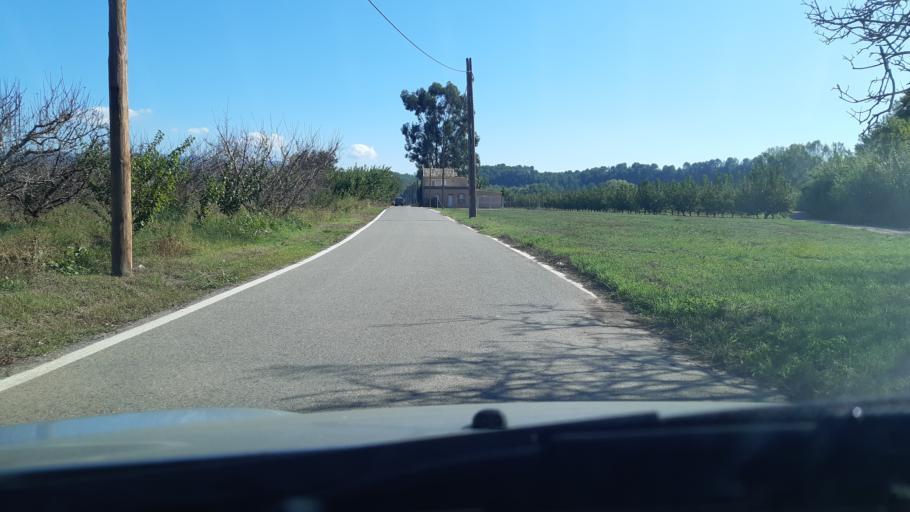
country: ES
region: Catalonia
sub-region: Provincia de Tarragona
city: Miravet
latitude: 41.0356
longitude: 0.6016
